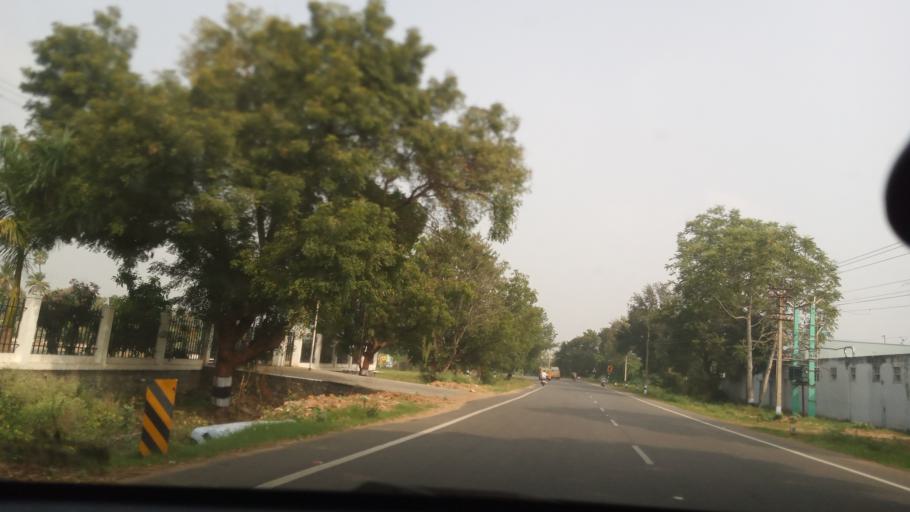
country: IN
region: Tamil Nadu
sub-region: Erode
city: Punjai Puliyampatti
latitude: 11.3677
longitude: 77.1713
